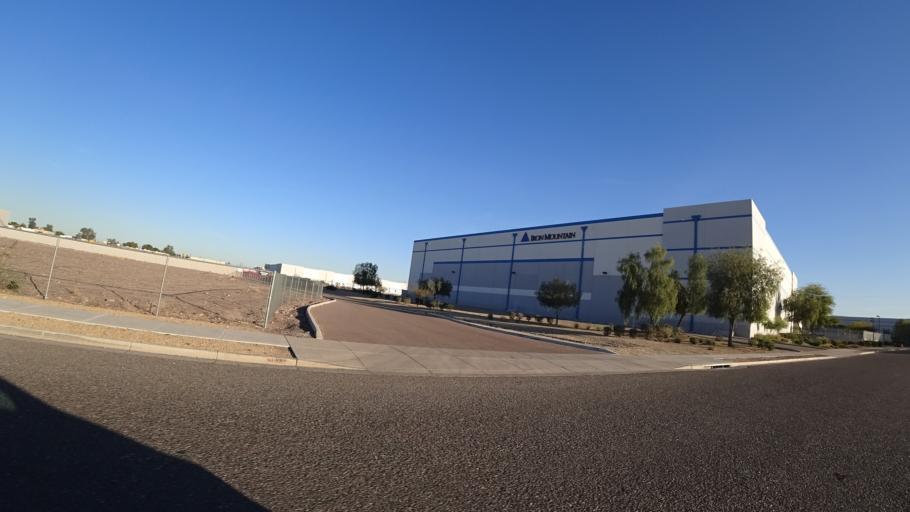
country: US
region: Arizona
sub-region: Maricopa County
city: Phoenix
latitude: 33.4212
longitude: -112.0424
